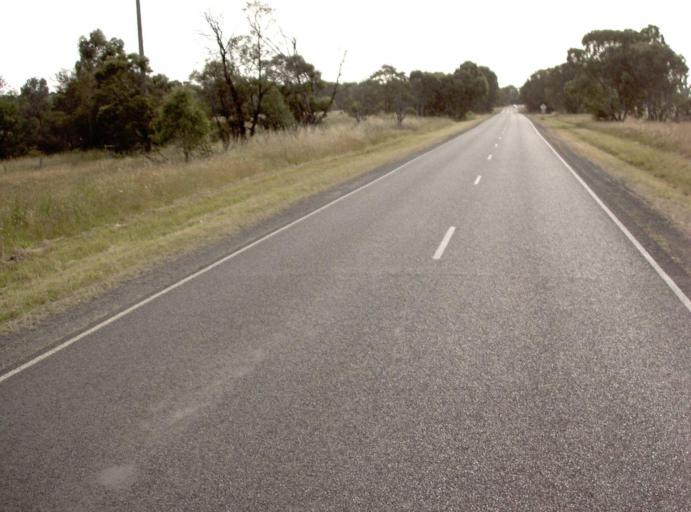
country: AU
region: Victoria
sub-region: Wellington
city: Heyfield
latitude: -38.0588
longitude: 146.6604
